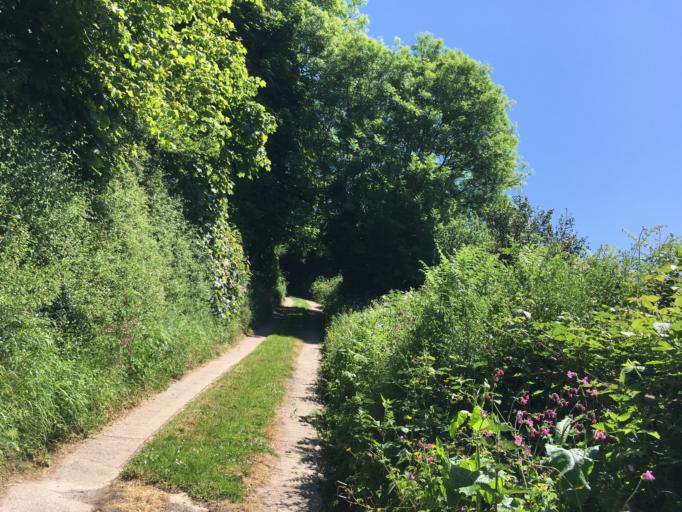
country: GB
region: England
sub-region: Devon
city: Dartmouth
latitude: 50.3451
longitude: -3.5478
